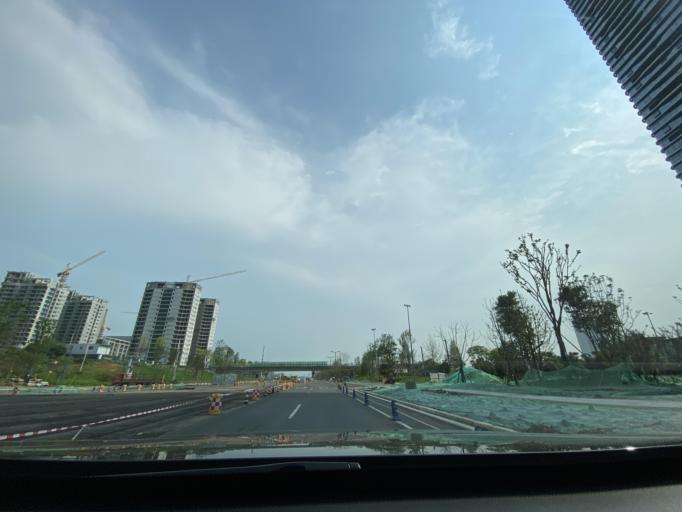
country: CN
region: Sichuan
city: Longquan
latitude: 30.4165
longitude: 104.1013
